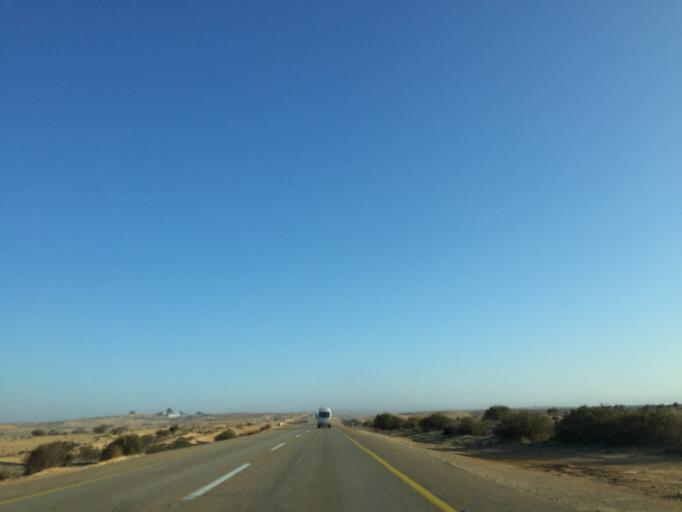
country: IL
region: Southern District
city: Yeroham
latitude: 31.0150
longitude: 34.9603
